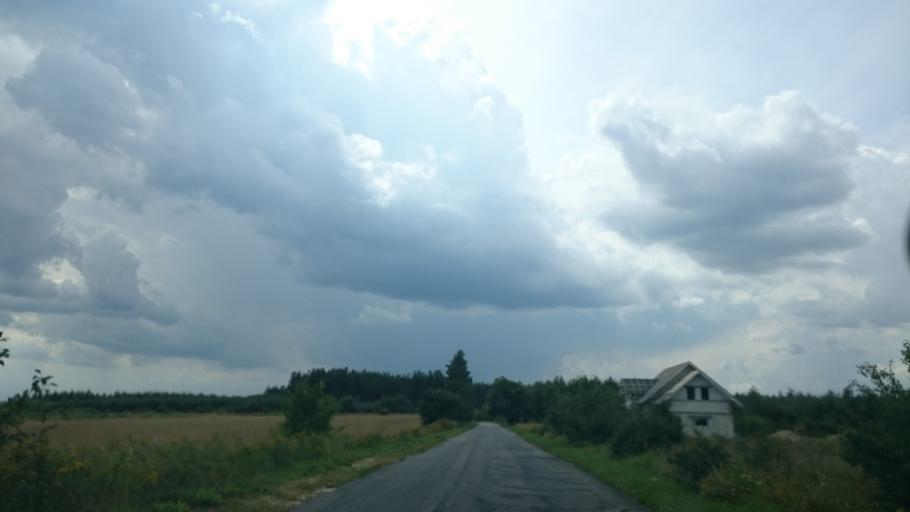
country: PL
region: Pomeranian Voivodeship
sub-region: Powiat chojnicki
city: Chojnice
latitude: 53.6961
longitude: 17.6823
